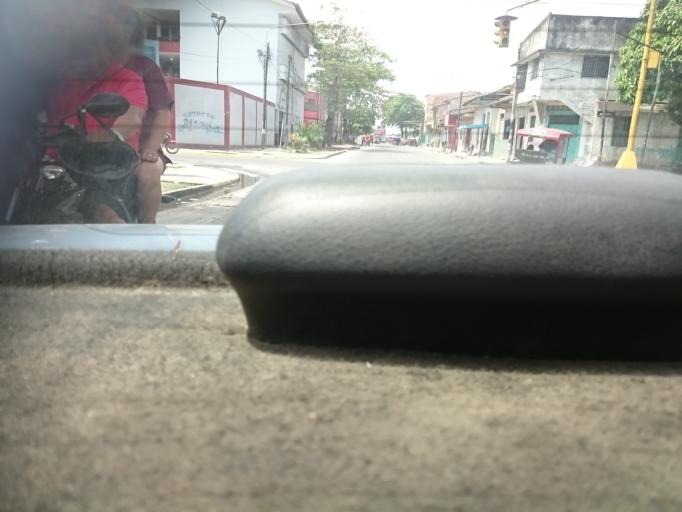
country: PE
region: Loreto
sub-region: Provincia de Maynas
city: Iquitos
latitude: -3.7607
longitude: -73.2550
